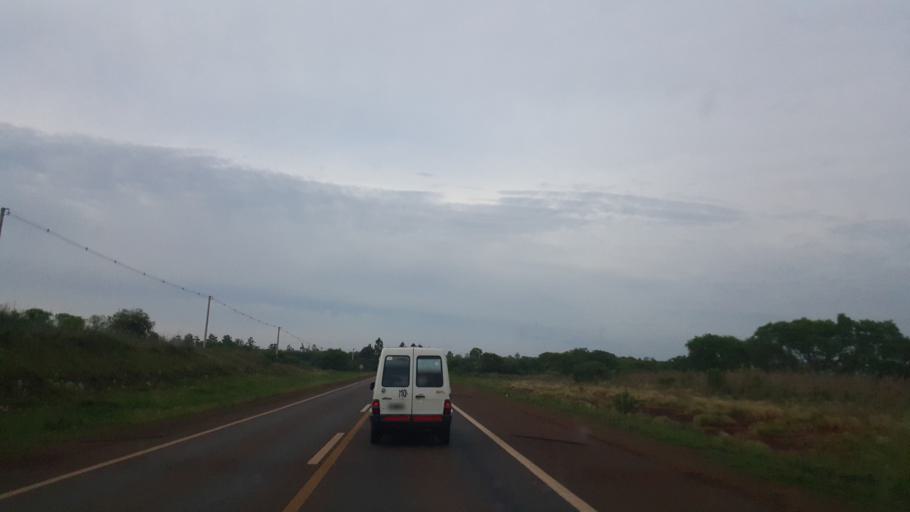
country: AR
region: Misiones
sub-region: Departamento de Apostoles
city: San Jose
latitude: -27.7767
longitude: -55.8100
